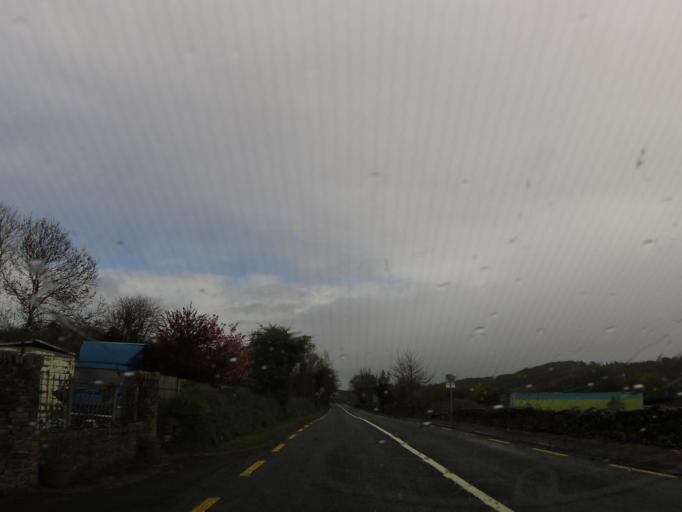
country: IE
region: Connaught
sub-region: Sligo
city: Collooney
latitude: 54.1922
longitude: -8.4939
